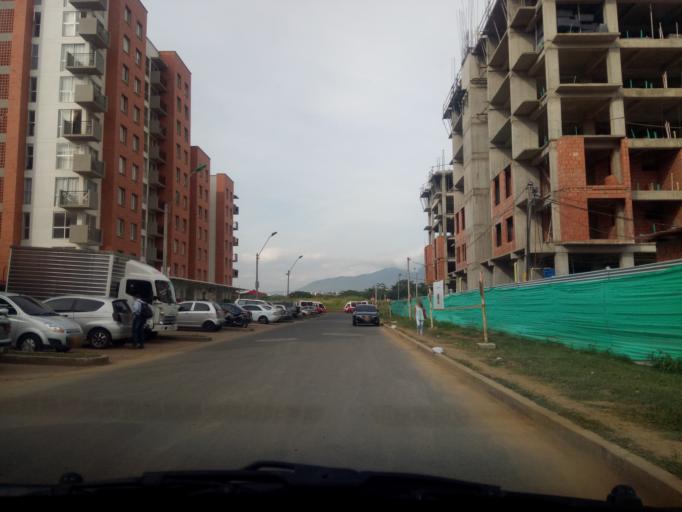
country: CO
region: Valle del Cauca
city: Cali
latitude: 3.3669
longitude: -76.5083
